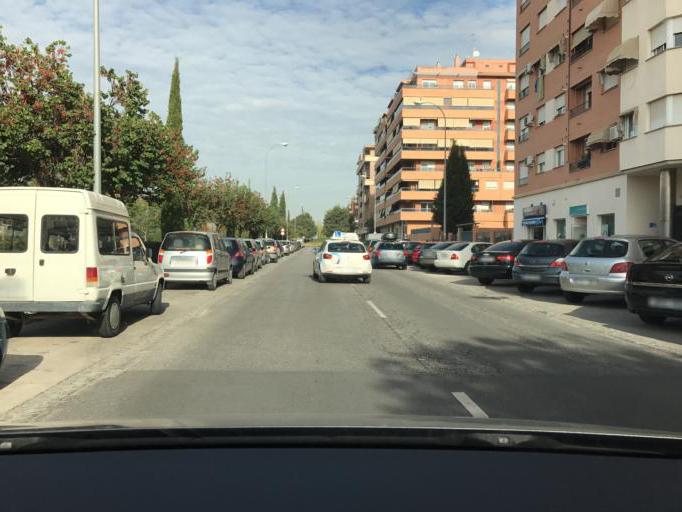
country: ES
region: Andalusia
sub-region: Provincia de Granada
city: Granada
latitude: 37.1981
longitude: -3.6153
